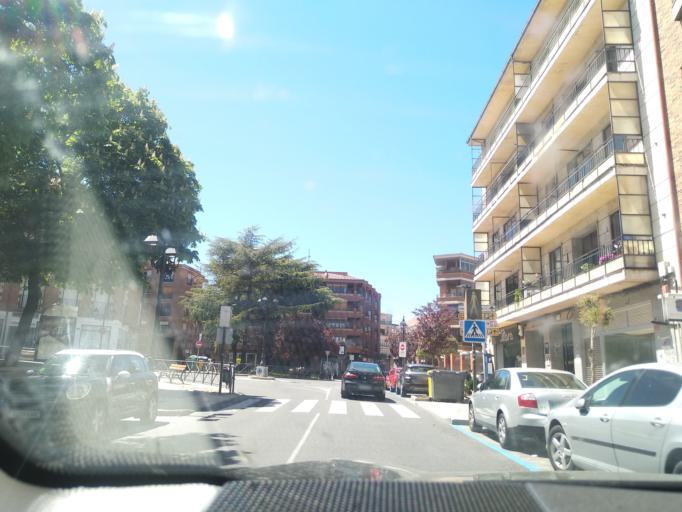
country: ES
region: Castille and Leon
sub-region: Provincia de Avila
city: Avila
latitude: 40.6573
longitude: -4.6914
